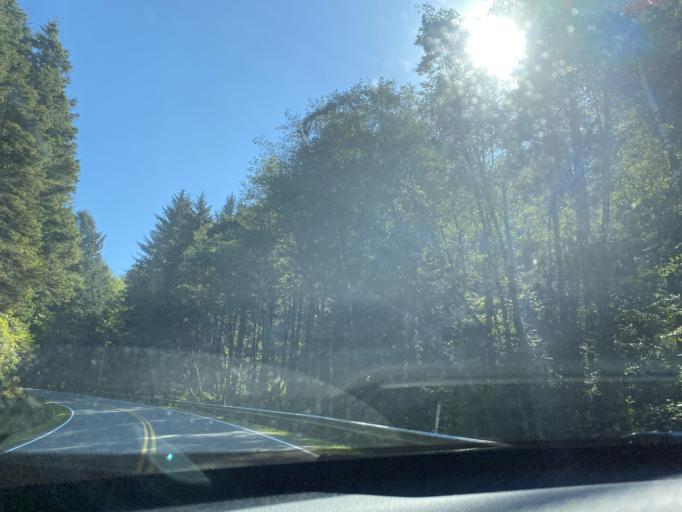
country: US
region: Washington
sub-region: Clallam County
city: Forks
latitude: 47.8989
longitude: -124.6257
